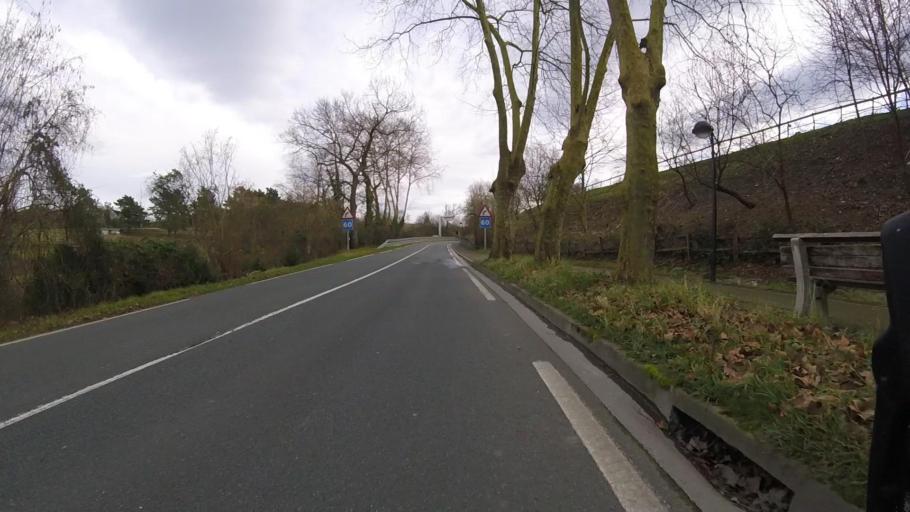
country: ES
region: Basque Country
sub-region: Provincia de Guipuzcoa
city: Lezo
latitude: 43.3054
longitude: -1.8776
